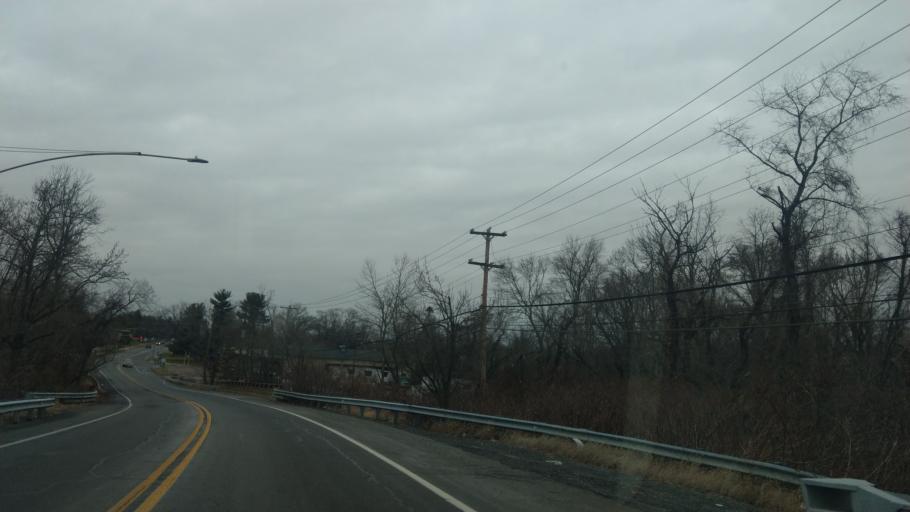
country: US
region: Pennsylvania
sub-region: Bucks County
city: Bristol
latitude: 40.1262
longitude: -74.8652
